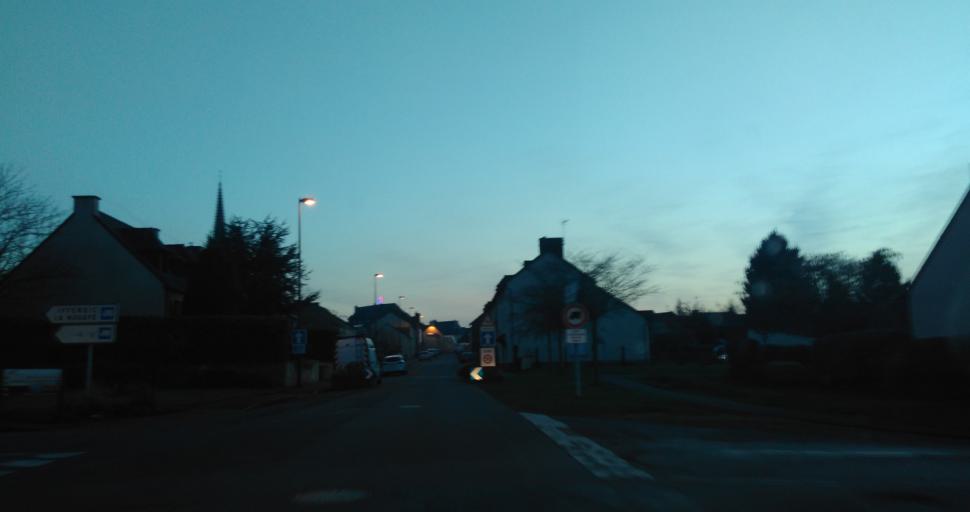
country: FR
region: Brittany
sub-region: Departement d'Ille-et-Vilaine
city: Bedee
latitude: 48.1825
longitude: -1.9449
